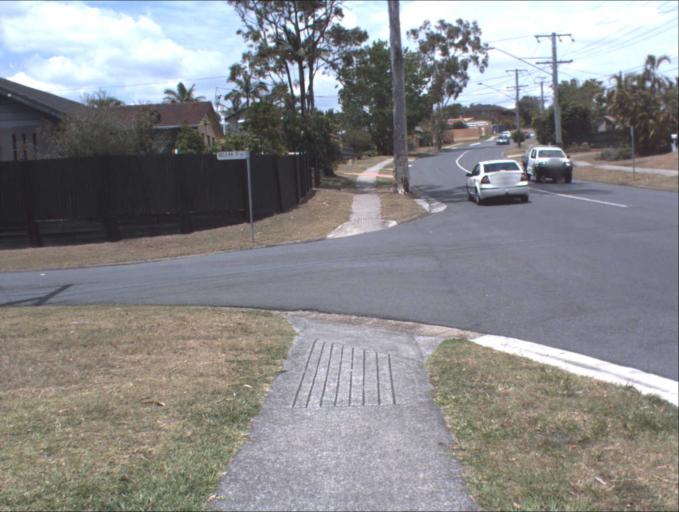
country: AU
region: Queensland
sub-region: Logan
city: Springwood
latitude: -27.6211
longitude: 153.1339
